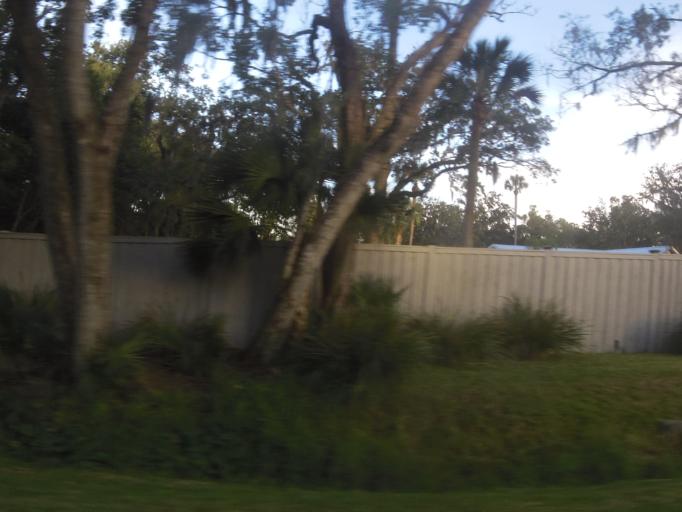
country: US
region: Florida
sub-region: Saint Johns County
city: Palm Valley
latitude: 30.1687
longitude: -81.3862
